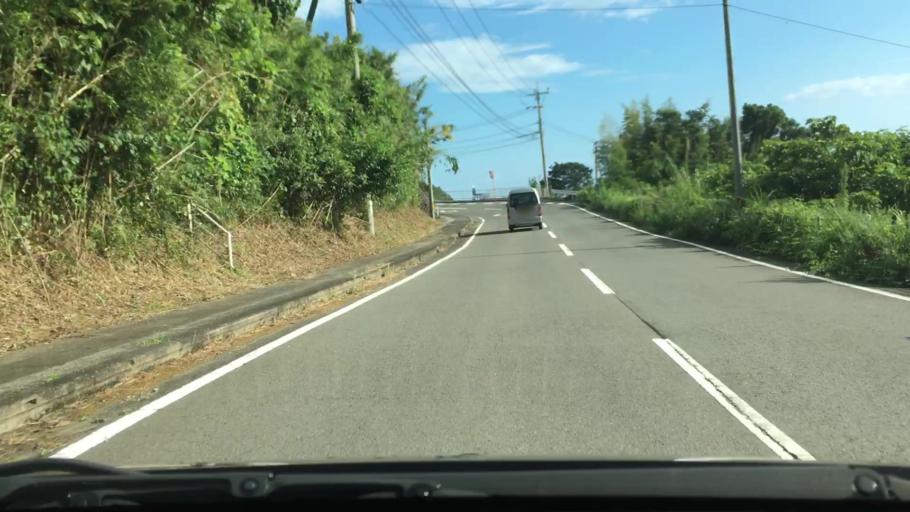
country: JP
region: Nagasaki
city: Togitsu
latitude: 32.8564
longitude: 129.6863
